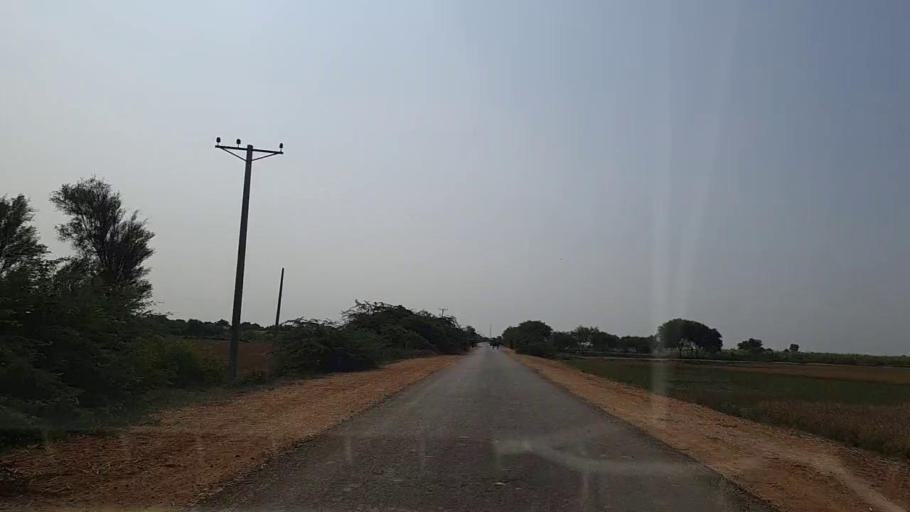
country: PK
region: Sindh
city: Chuhar Jamali
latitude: 24.3014
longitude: 67.9334
